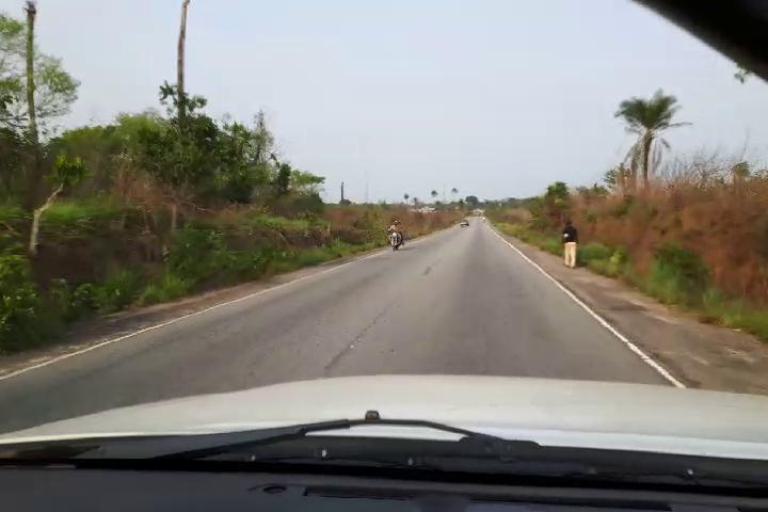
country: SL
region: Southern Province
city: Baoma
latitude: 7.9278
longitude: -11.5829
